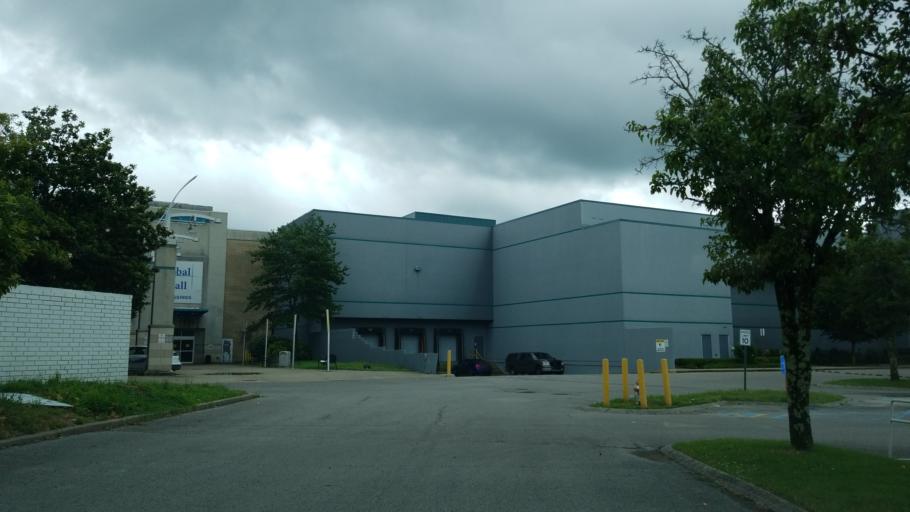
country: US
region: Tennessee
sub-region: Rutherford County
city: La Vergne
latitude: 36.0507
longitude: -86.6575
